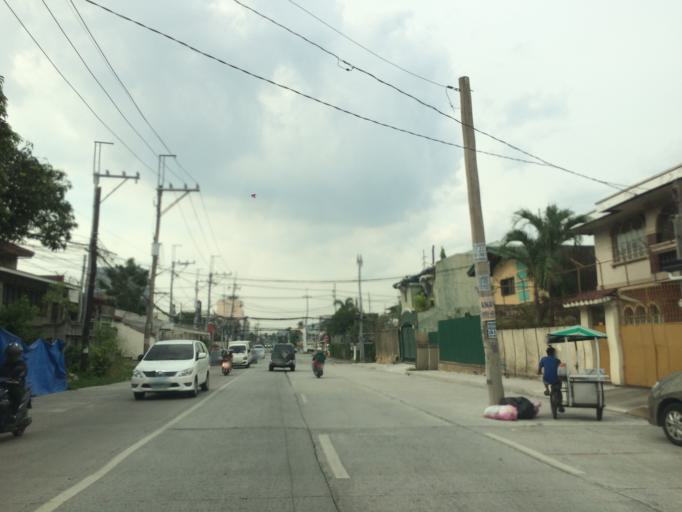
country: PH
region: Calabarzon
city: Del Monte
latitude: 14.6375
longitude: 121.0055
